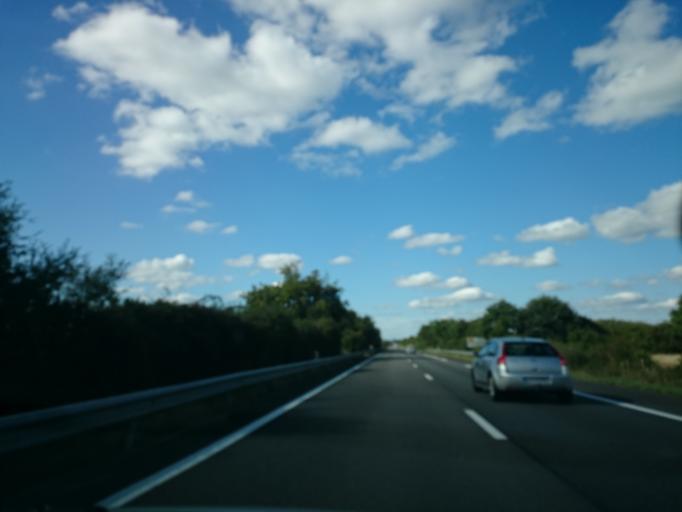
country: FR
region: Pays de la Loire
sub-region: Departement de la Loire-Atlantique
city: La Grigonnais
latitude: 47.4786
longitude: -1.6365
